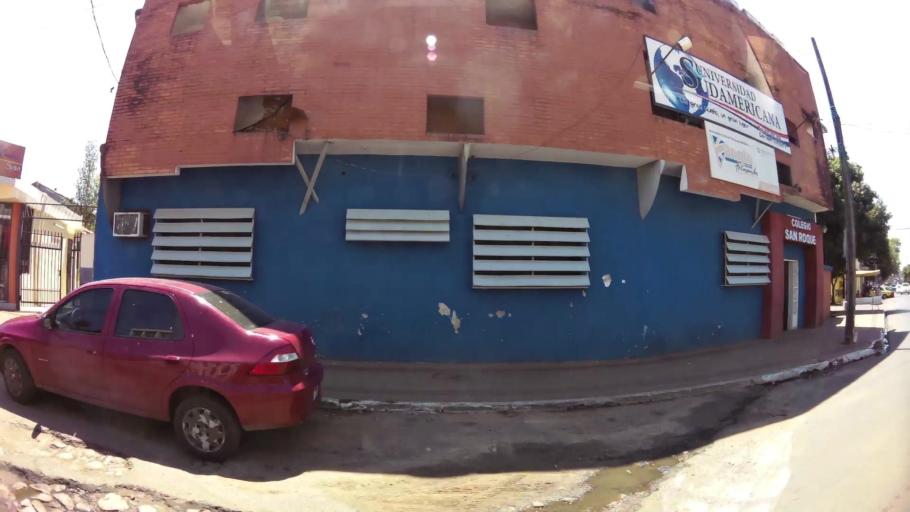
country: PY
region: Central
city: Fernando de la Mora
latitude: -25.3239
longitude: -57.5586
